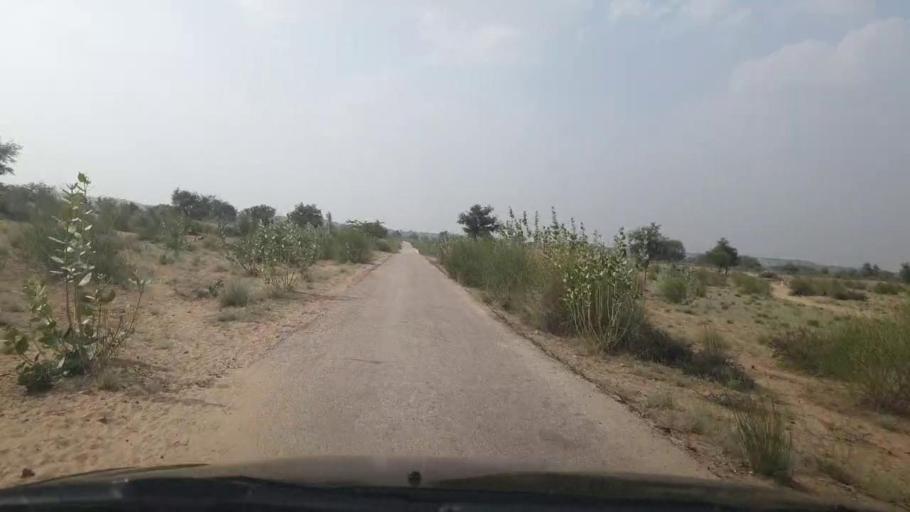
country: PK
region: Sindh
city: Islamkot
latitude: 24.9621
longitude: 70.6304
